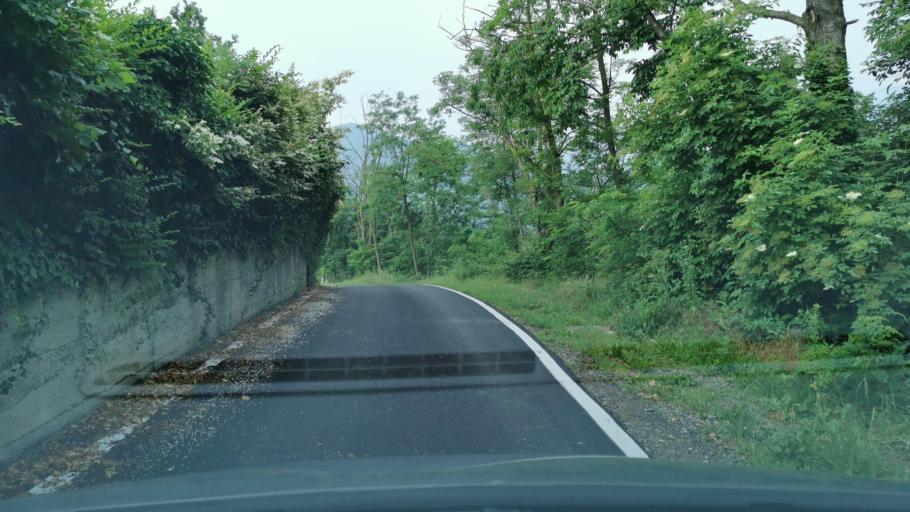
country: IT
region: Piedmont
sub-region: Provincia di Torino
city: Vallo Torinese
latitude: 45.2122
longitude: 7.5006
